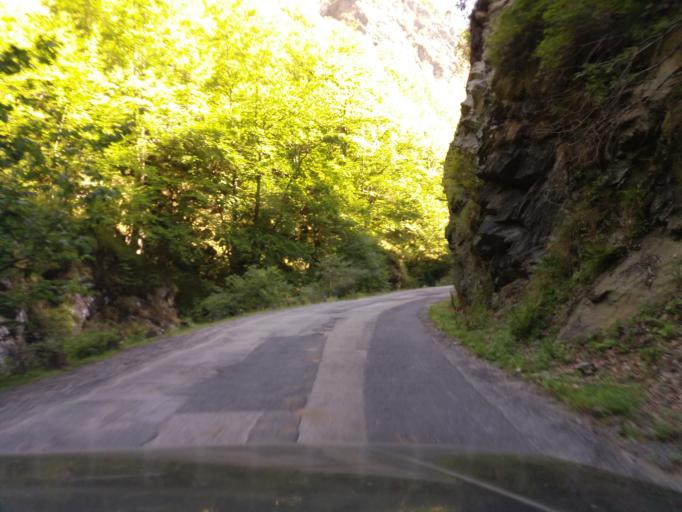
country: RO
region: Hunedoara
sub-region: Oras Petrila
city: Petrila
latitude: 45.4122
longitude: 23.4670
